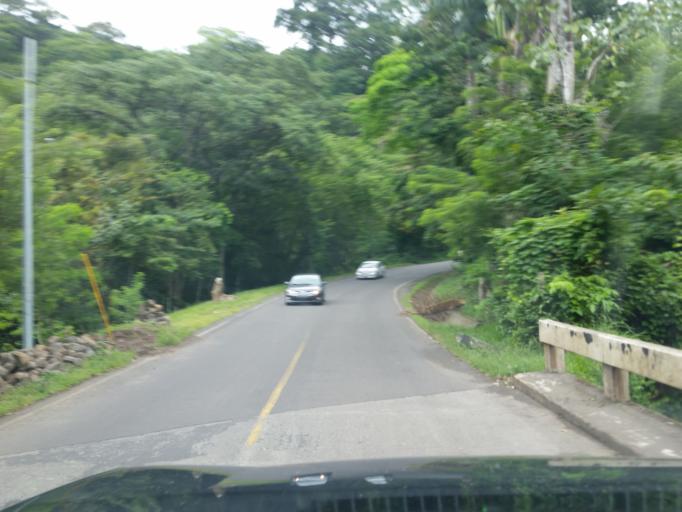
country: NI
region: Matagalpa
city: San Ramon
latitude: 12.9912
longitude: -85.8331
